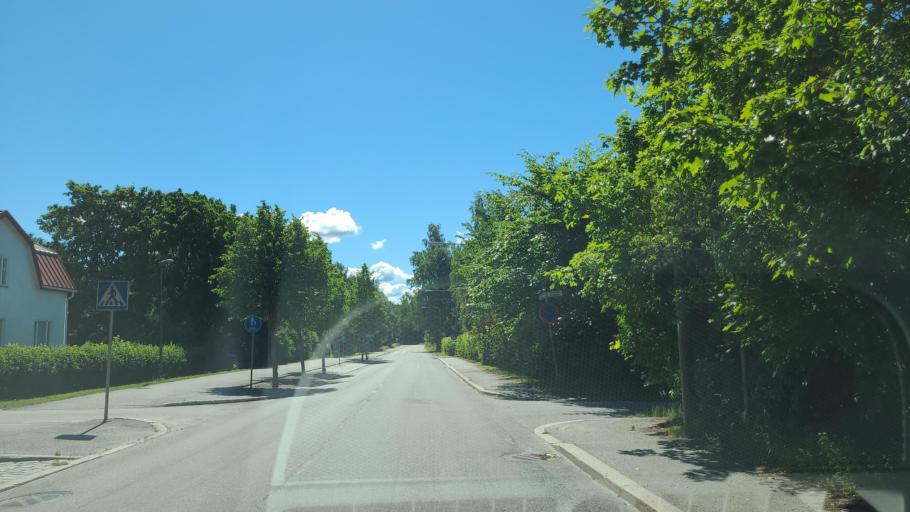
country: FI
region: Ostrobothnia
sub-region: Vaasa
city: Ristinummi
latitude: 63.0713
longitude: 21.7231
